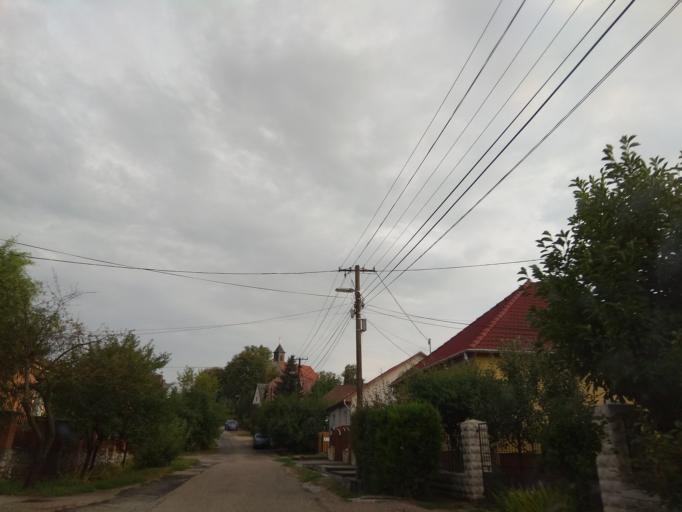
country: HU
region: Borsod-Abauj-Zemplen
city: Miskolc
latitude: 48.0591
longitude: 20.7862
